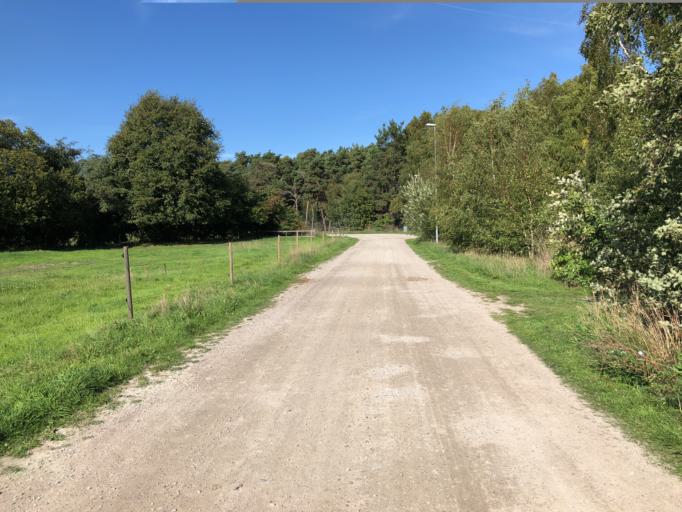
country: SE
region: Skane
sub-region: Lomma Kommun
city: Lomma
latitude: 55.6874
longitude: 13.0700
